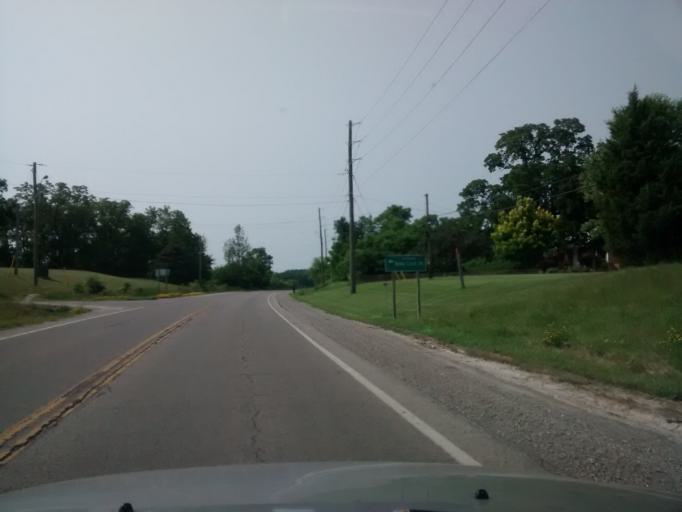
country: CA
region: Ontario
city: Ancaster
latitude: 43.0508
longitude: -79.9117
